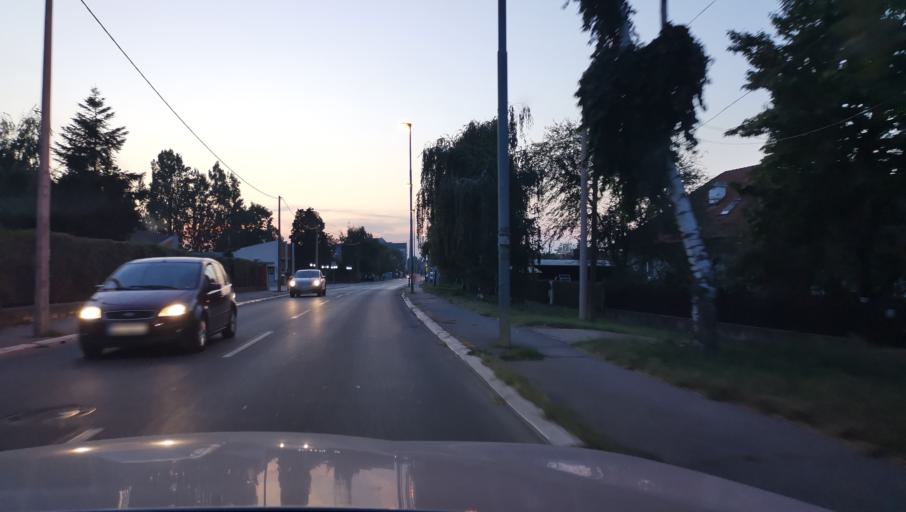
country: RS
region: Central Serbia
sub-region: Belgrade
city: Obrenovac
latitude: 44.6657
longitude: 20.1961
